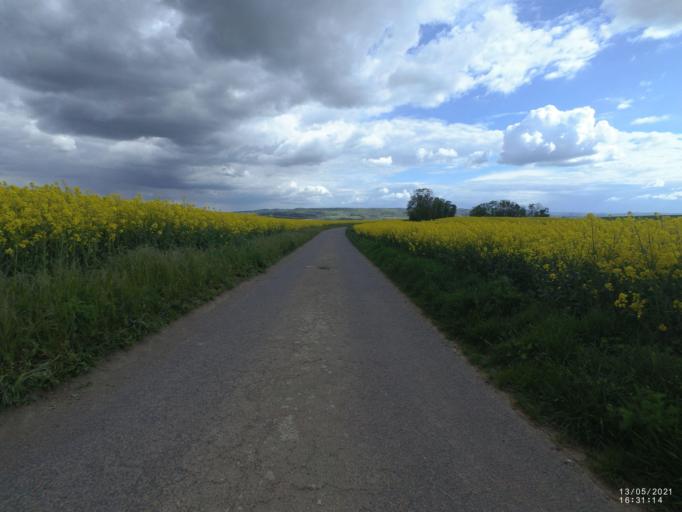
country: DE
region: Rheinland-Pfalz
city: Wolken
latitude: 50.3258
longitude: 7.4639
